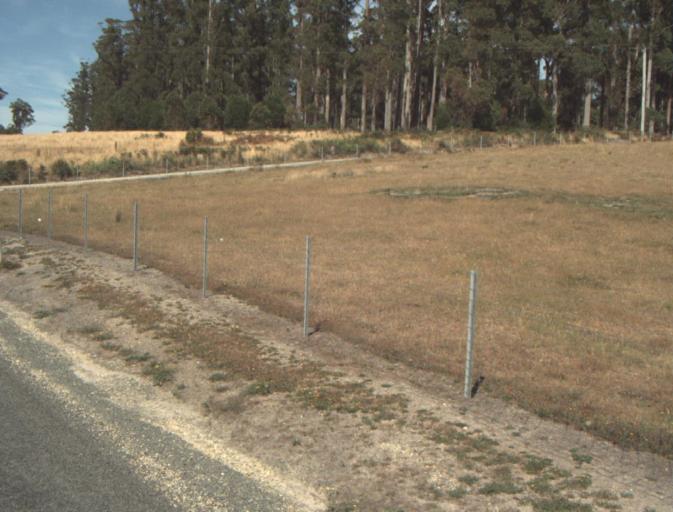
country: AU
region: Tasmania
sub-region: Launceston
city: Mayfield
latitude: -41.2304
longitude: 147.2356
